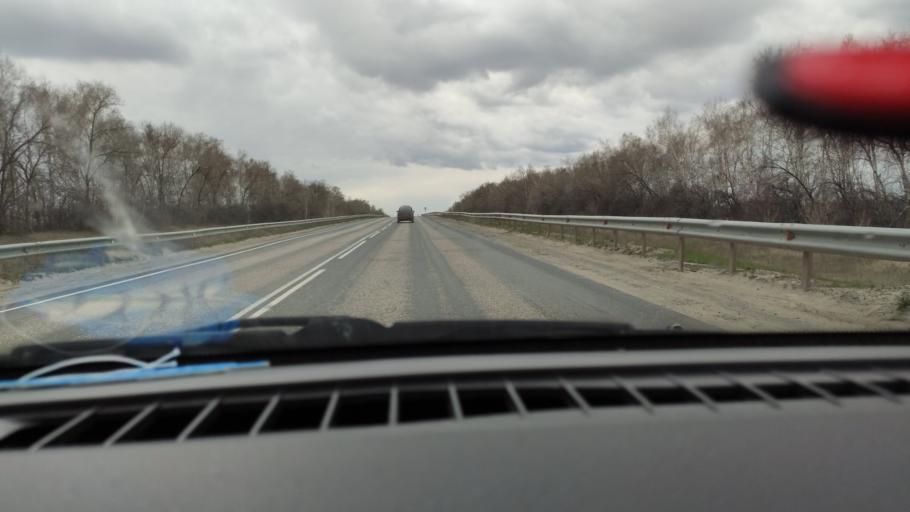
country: RU
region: Saratov
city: Sinodskoye
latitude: 51.9581
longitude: 46.6192
